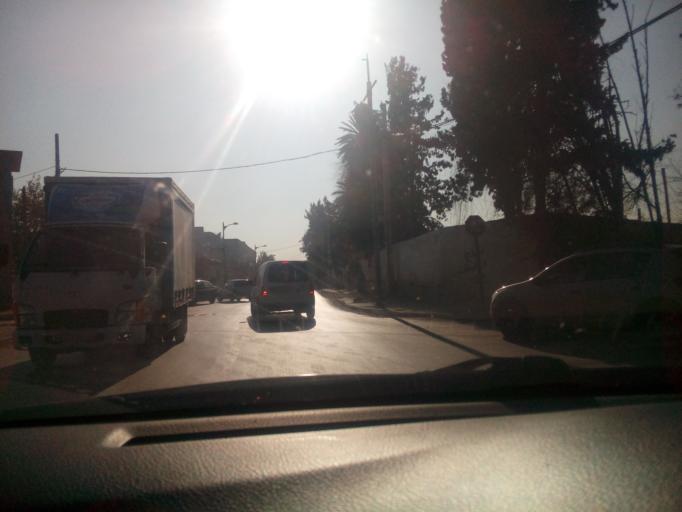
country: DZ
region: Oran
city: Es Senia
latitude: 35.6463
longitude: -0.6250
